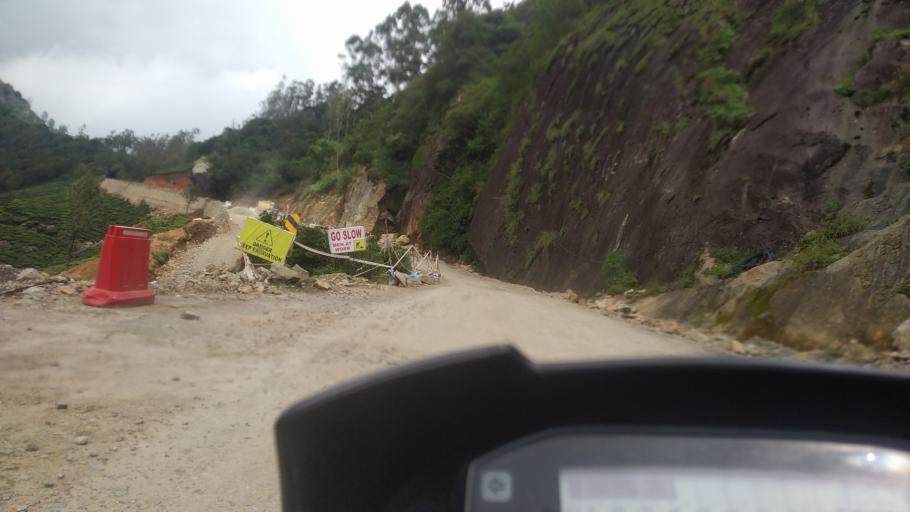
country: IN
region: Kerala
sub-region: Idukki
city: Munnar
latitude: 10.0362
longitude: 77.1175
